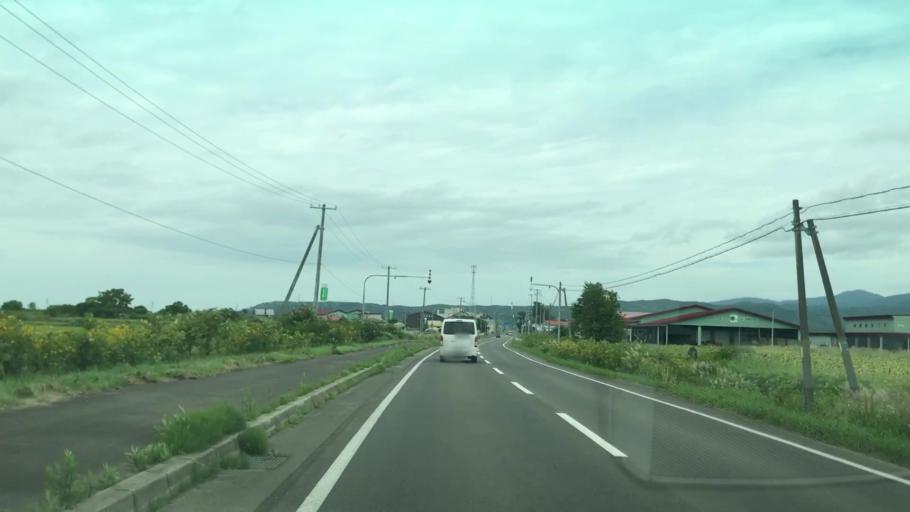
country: JP
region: Hokkaido
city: Iwanai
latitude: 43.0124
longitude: 140.5734
